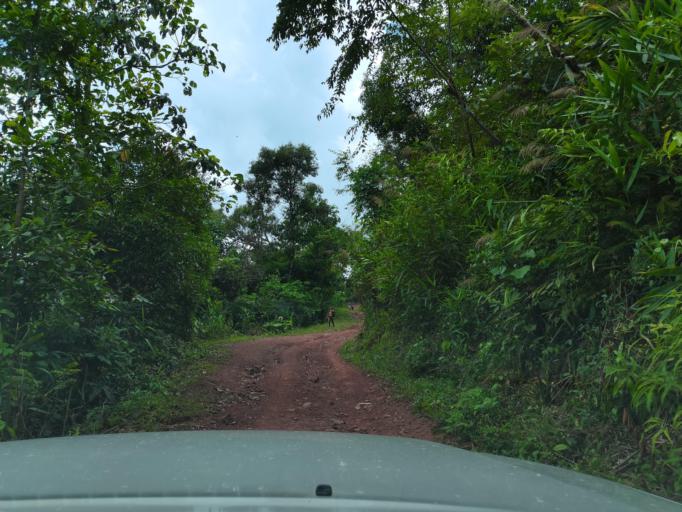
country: LA
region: Loungnamtha
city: Muang Nale
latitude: 20.5064
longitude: 101.0846
